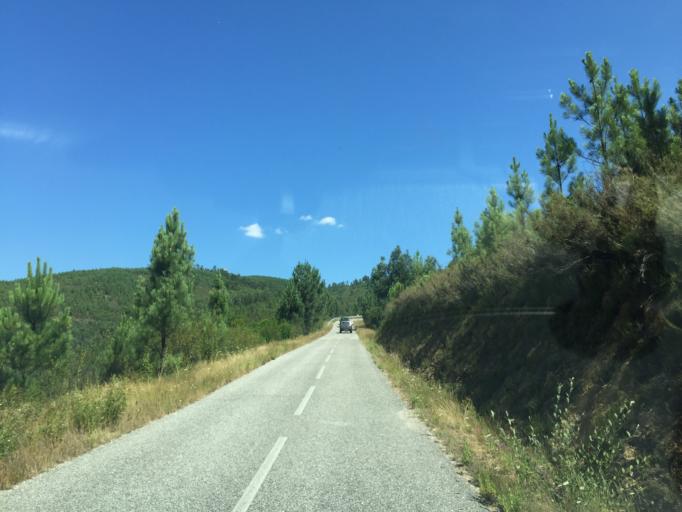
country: PT
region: Coimbra
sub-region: Pampilhosa da Serra
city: Pampilhosa da Serra
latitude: 40.0826
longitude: -7.8255
